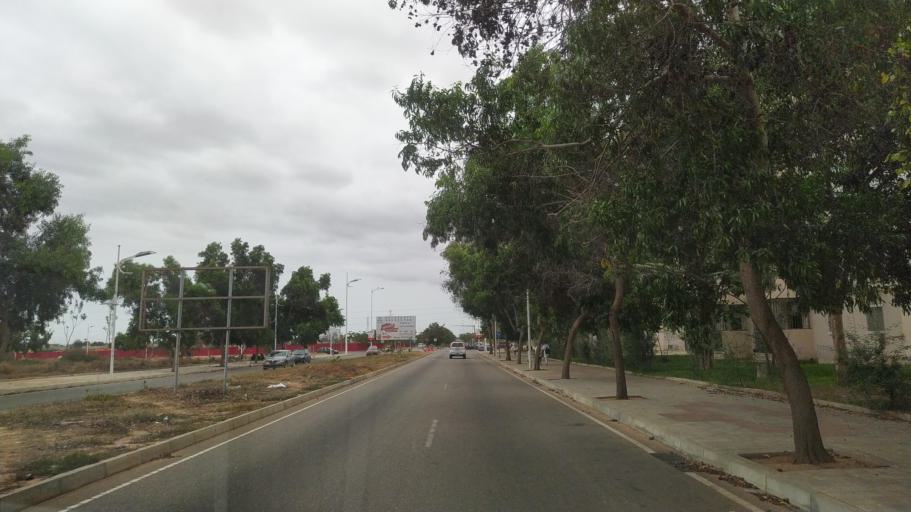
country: AO
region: Luanda
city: Luanda
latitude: -8.9925
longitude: 13.2521
